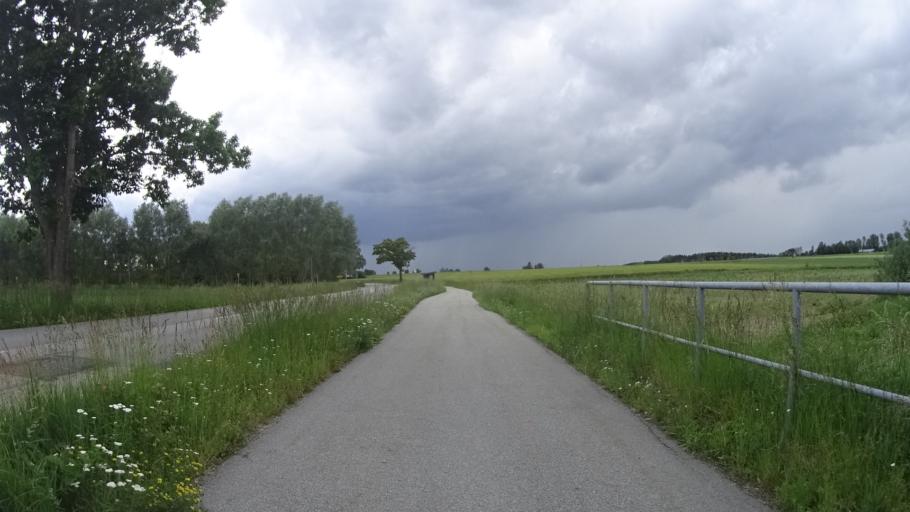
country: DE
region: Bavaria
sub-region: Upper Bavaria
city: Egglkofen
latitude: 48.4478
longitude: 12.4816
